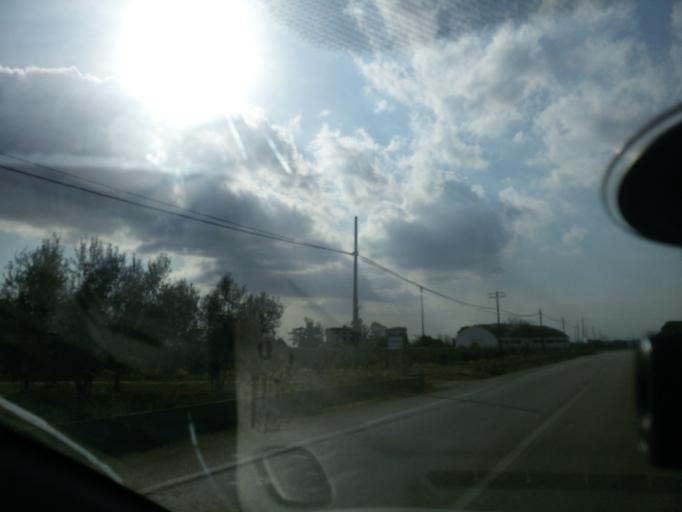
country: IT
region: Apulia
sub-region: Provincia di Brindisi
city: Mesagne
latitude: 40.6513
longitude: 17.8215
